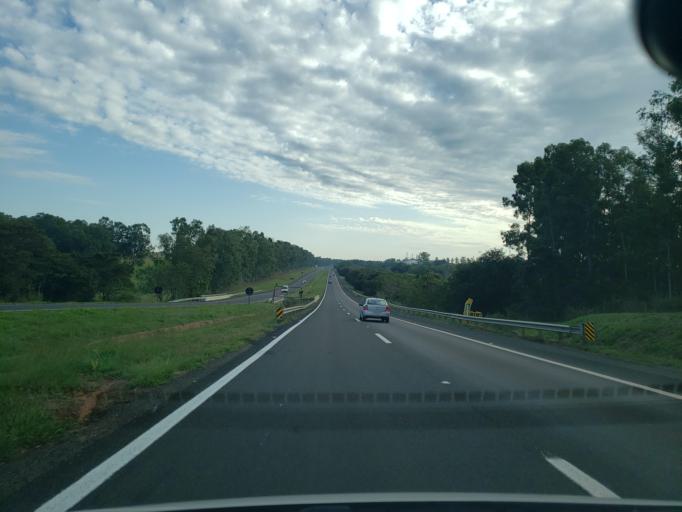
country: BR
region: Sao Paulo
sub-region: Guararapes
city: Guararapes
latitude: -21.2105
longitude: -50.6710
